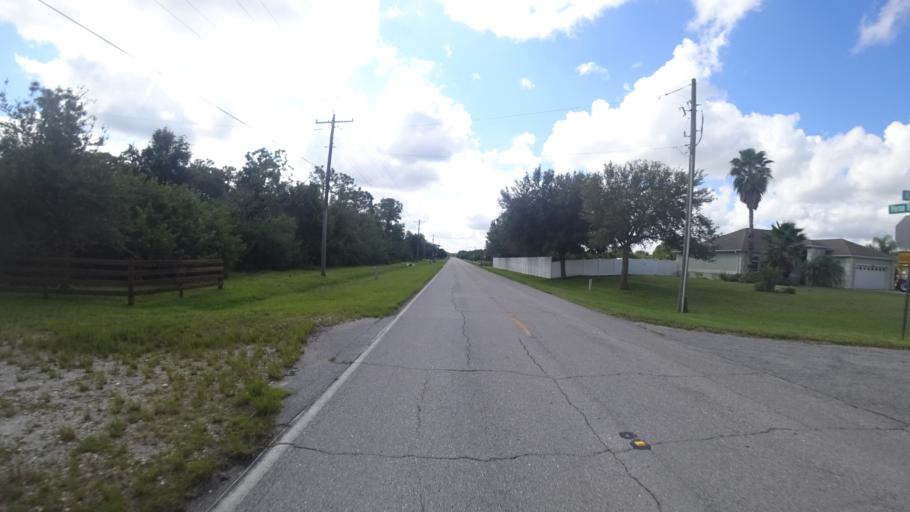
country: US
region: Florida
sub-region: Sarasota County
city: Lake Sarasota
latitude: 27.3946
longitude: -82.2712
